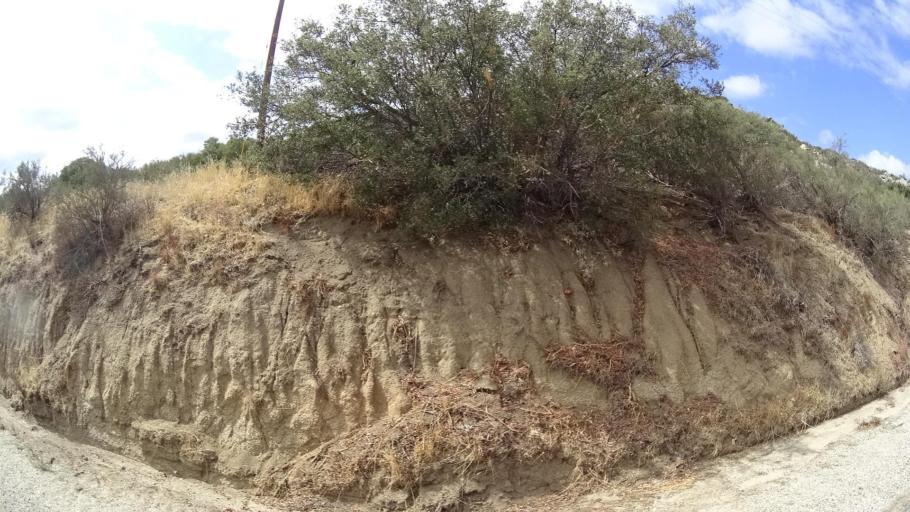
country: US
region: California
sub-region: San Diego County
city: Campo
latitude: 32.6788
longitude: -116.4887
